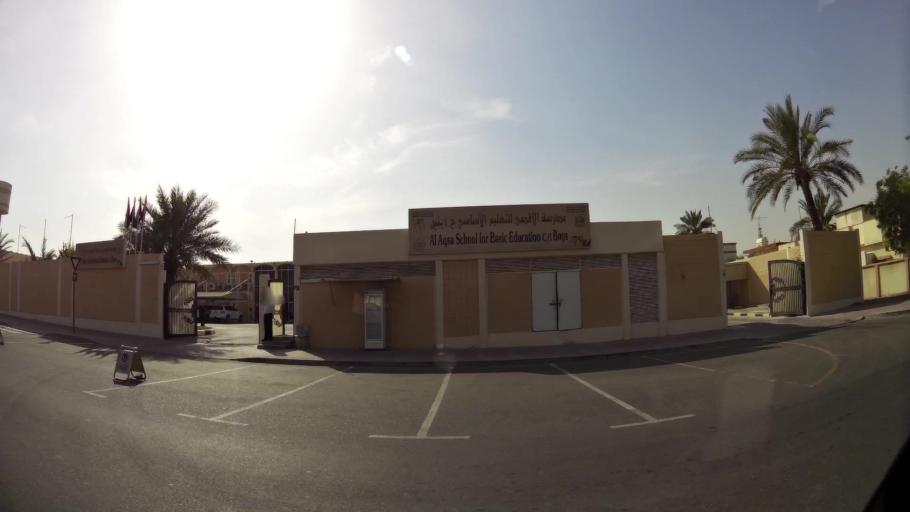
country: AE
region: Ash Shariqah
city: Sharjah
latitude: 25.2228
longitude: 55.3931
